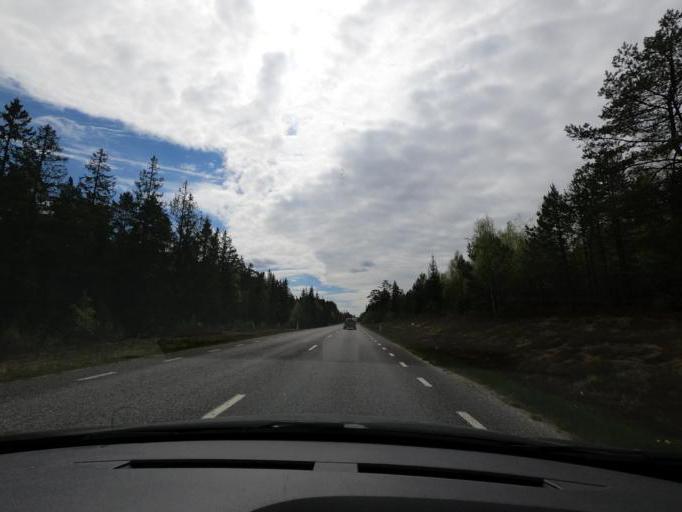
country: SE
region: Vaestra Goetaland
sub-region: Tranemo Kommun
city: Tranemo
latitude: 57.4207
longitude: 13.4513
